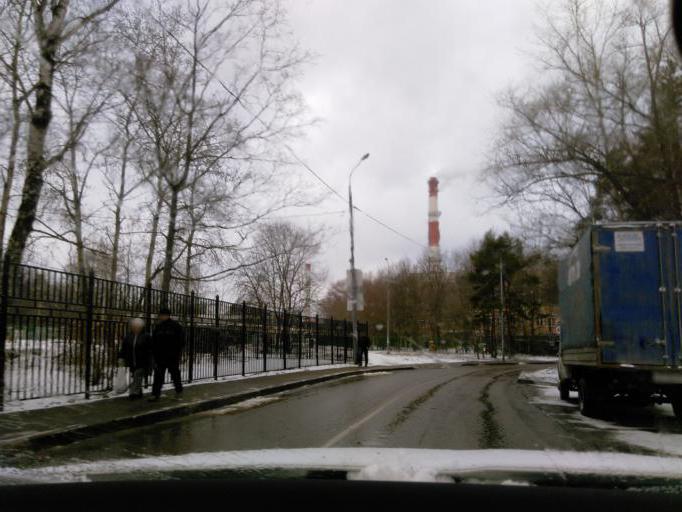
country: RU
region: Moscow
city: Zelenograd
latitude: 56.0033
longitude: 37.2016
